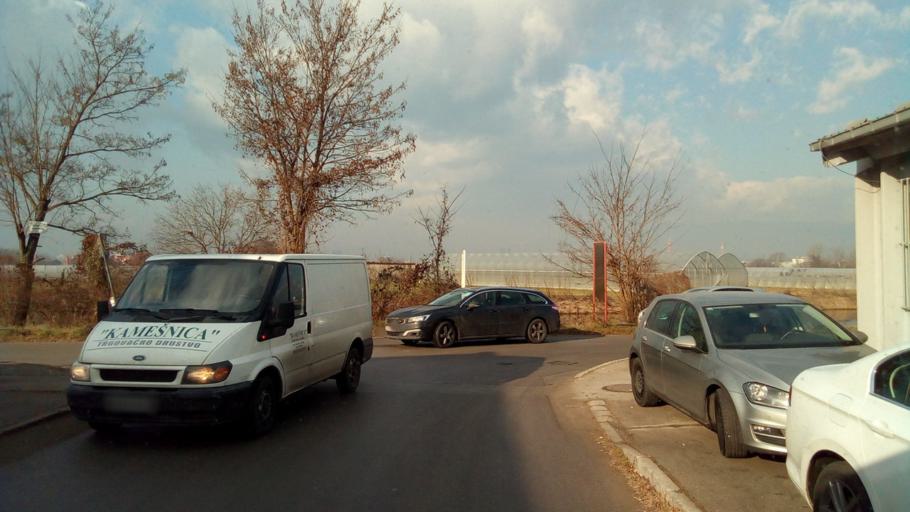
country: HR
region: Grad Zagreb
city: Novi Zagreb
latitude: 45.7855
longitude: 16.0280
